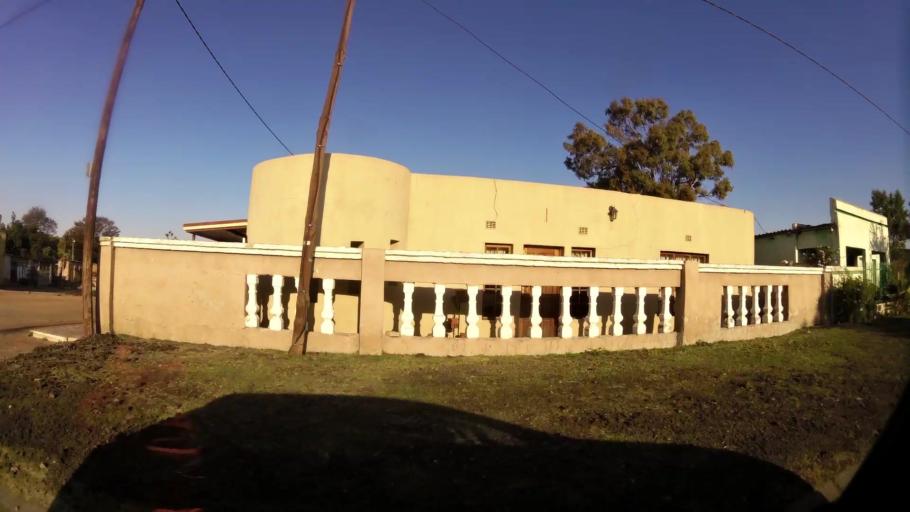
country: ZA
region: North-West
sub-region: Bojanala Platinum District Municipality
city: Rustenburg
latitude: -25.6377
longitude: 27.2195
